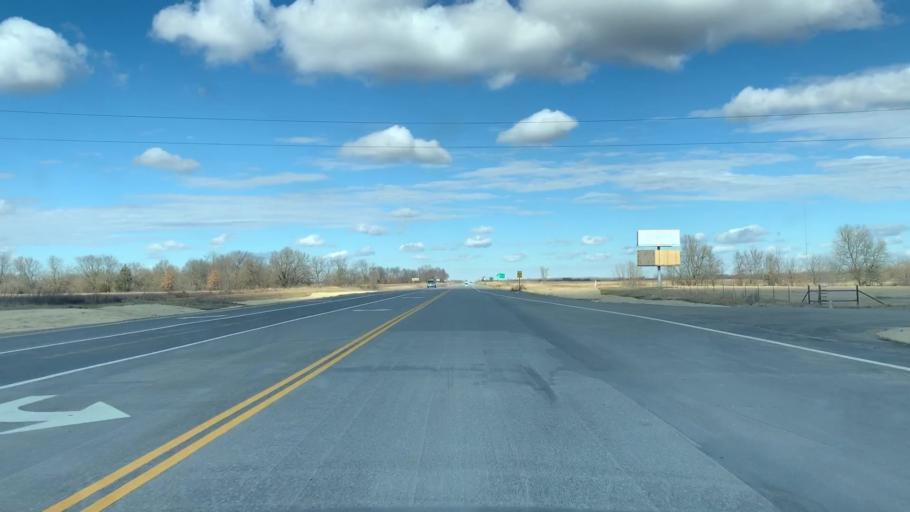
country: US
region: Kansas
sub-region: Cherokee County
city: Columbus
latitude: 37.2817
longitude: -94.8322
